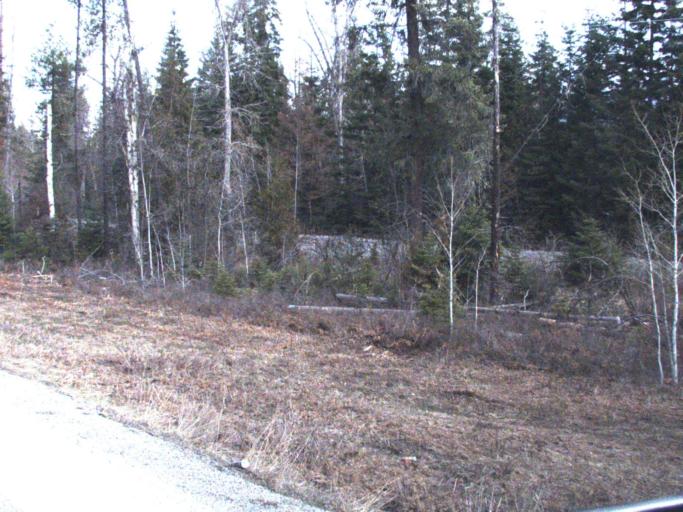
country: US
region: Washington
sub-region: Stevens County
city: Chewelah
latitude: 48.5992
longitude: -117.3599
